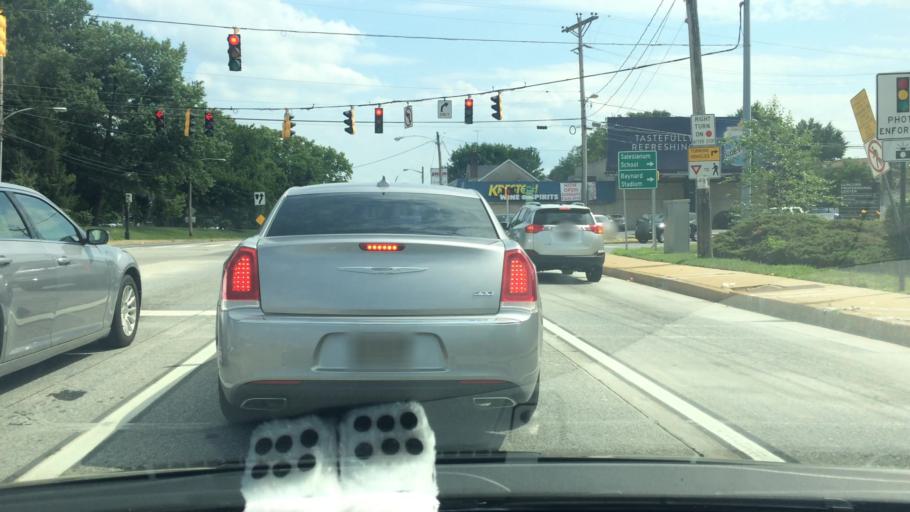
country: US
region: Delaware
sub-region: New Castle County
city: Wilmington
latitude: 39.7637
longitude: -75.5427
